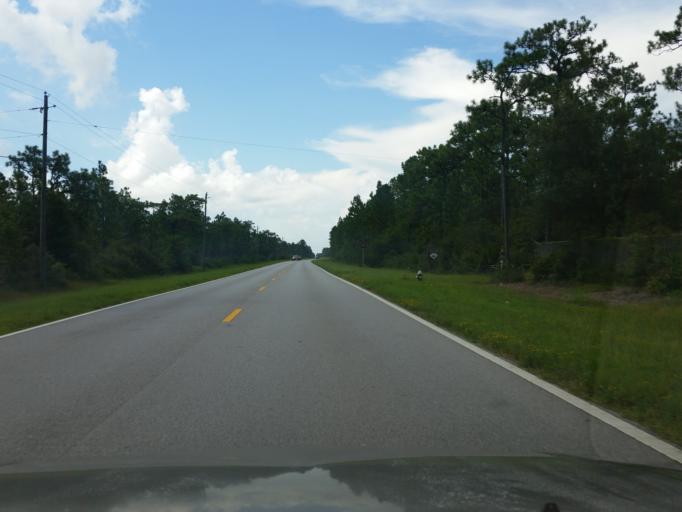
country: US
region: Florida
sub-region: Escambia County
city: Myrtle Grove
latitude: 30.3763
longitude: -87.4022
